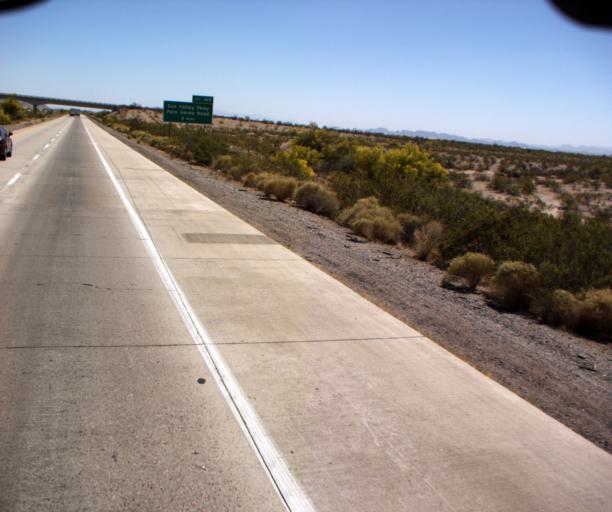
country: US
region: Arizona
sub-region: Maricopa County
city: Buckeye
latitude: 33.4476
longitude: -112.7153
